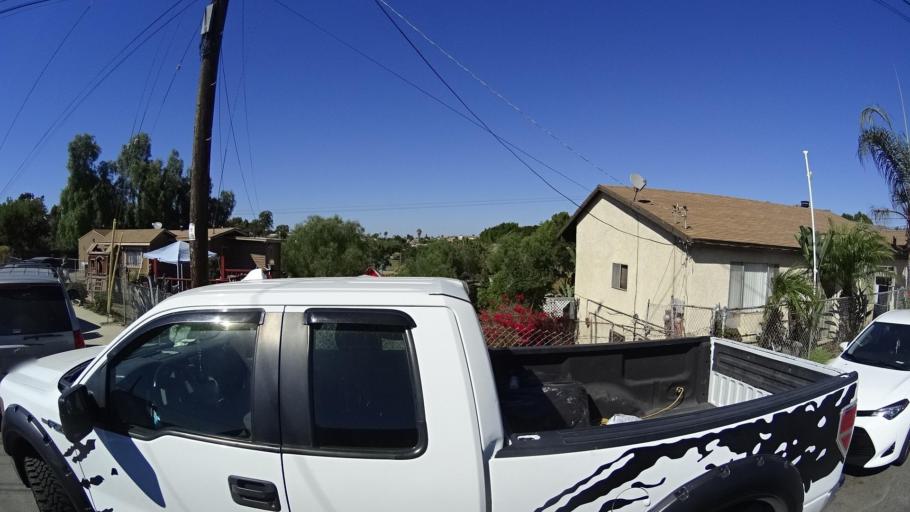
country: US
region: California
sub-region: San Diego County
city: National City
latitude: 32.6687
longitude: -117.0760
